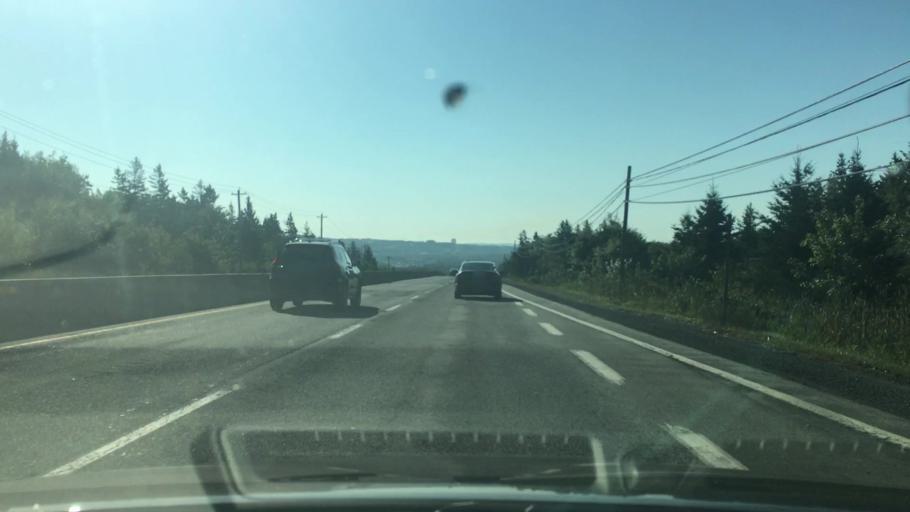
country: CA
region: Nova Scotia
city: Dartmouth
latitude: 44.7173
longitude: -63.6342
